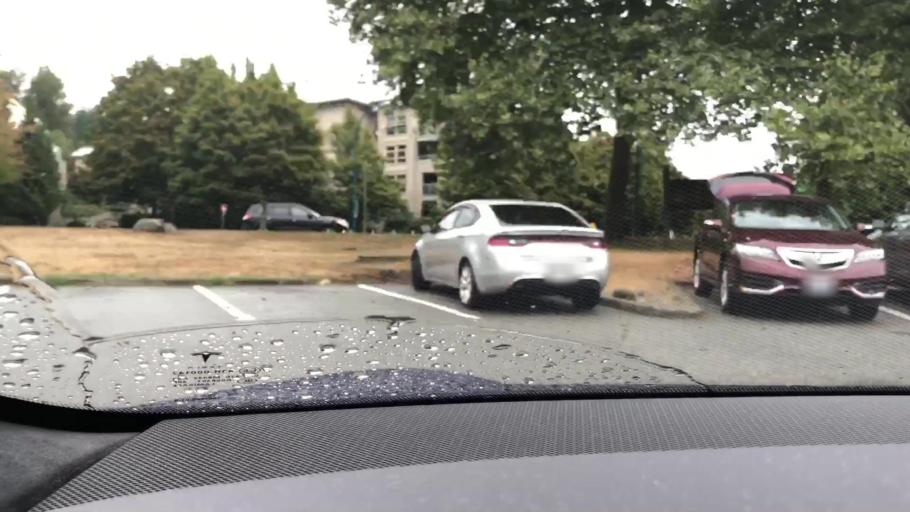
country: CA
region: British Columbia
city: Port Moody
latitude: 49.2837
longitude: -122.8307
